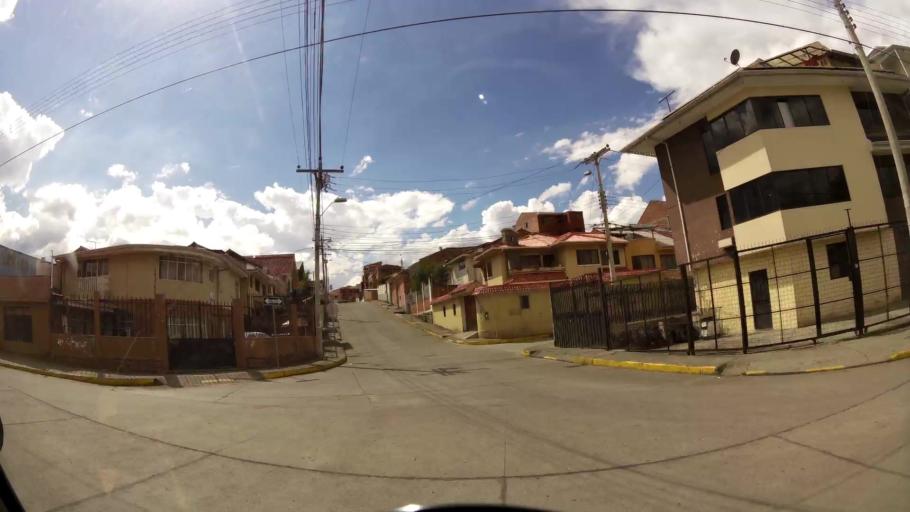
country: EC
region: Azuay
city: Cuenca
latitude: -2.8832
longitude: -78.9857
